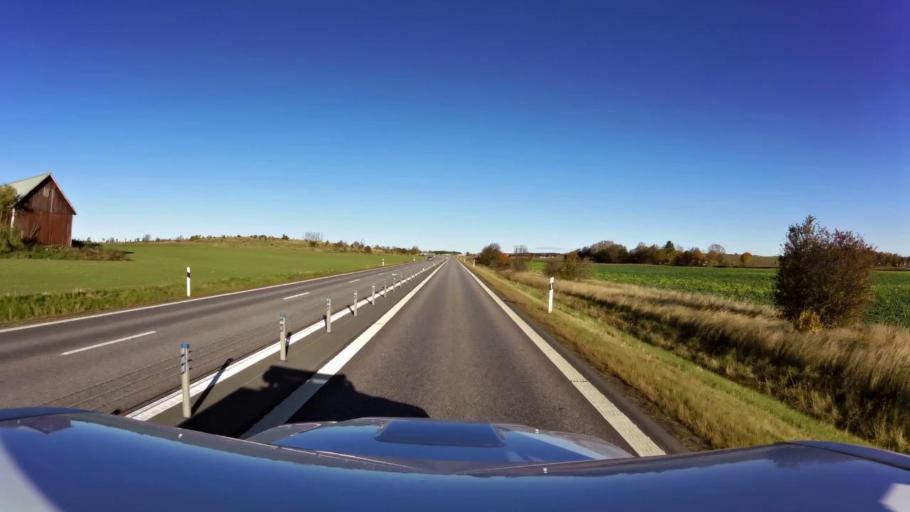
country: SE
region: OEstergoetland
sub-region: Linkopings Kommun
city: Berg
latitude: 58.4723
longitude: 15.4912
